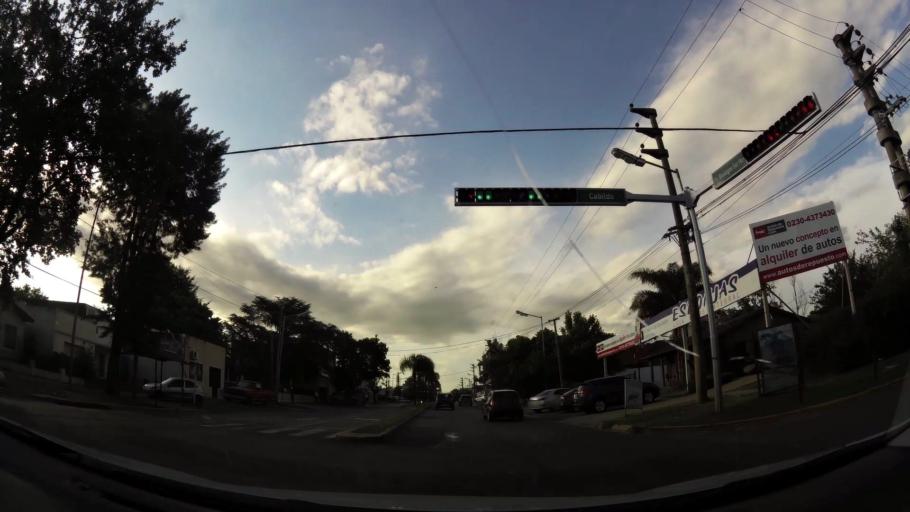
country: AR
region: Buenos Aires
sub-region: Partido de Tigre
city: Tigre
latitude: -34.4636
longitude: -58.6273
